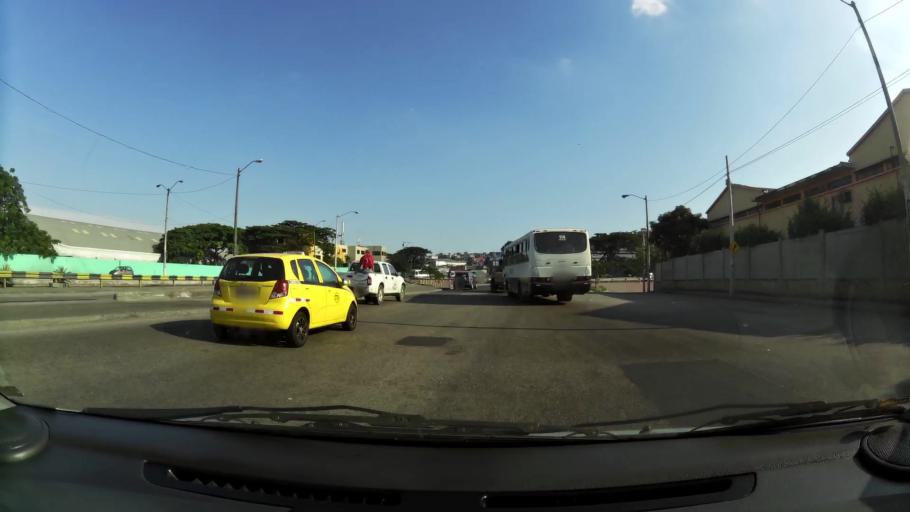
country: EC
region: Guayas
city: Guayaquil
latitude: -2.1482
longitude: -79.9120
